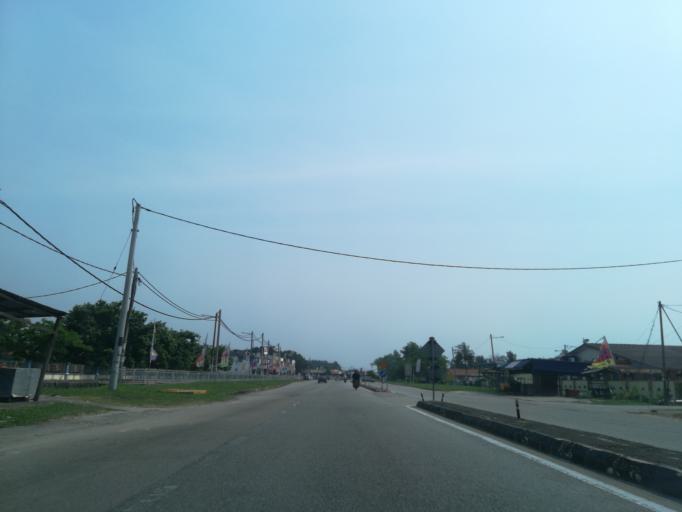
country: MY
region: Kedah
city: Kulim
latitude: 5.4189
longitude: 100.5499
